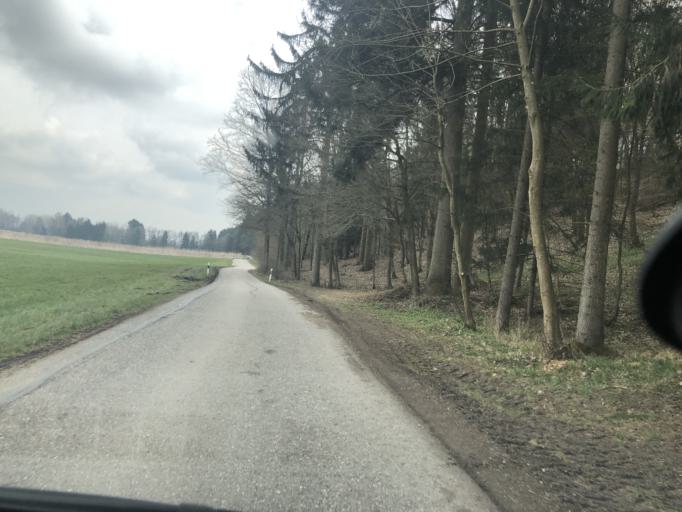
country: DE
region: Bavaria
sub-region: Upper Bavaria
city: Zolling
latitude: 48.4402
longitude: 11.7374
